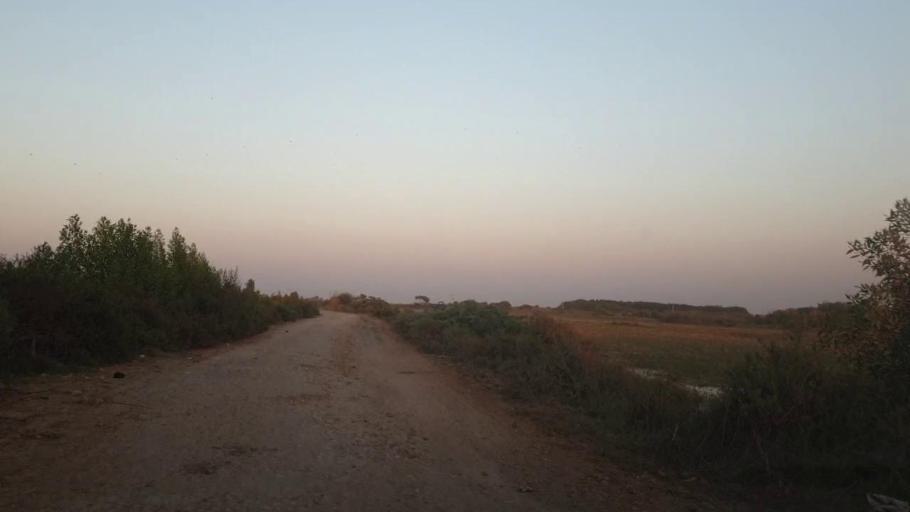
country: PK
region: Sindh
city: Mirpur Sakro
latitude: 24.4237
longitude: 67.5945
